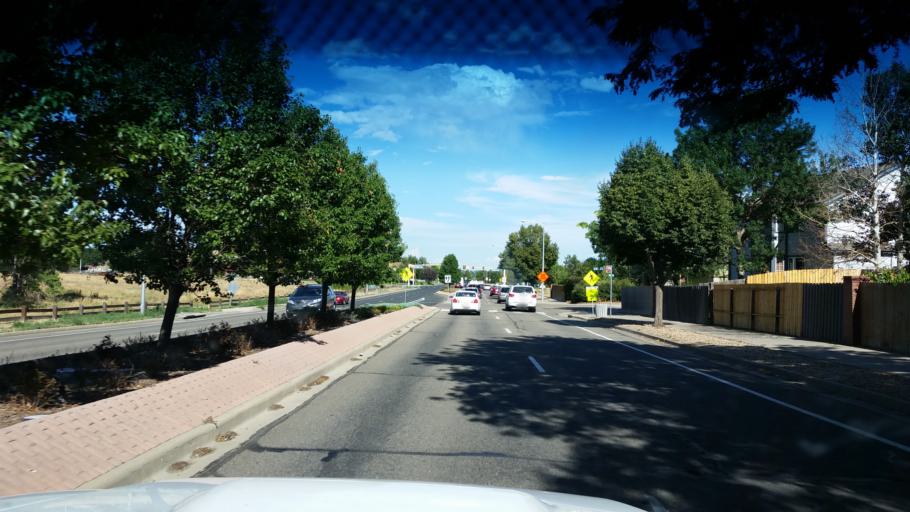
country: US
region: Colorado
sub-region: Broomfield County
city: Broomfield
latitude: 39.9287
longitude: -105.0372
